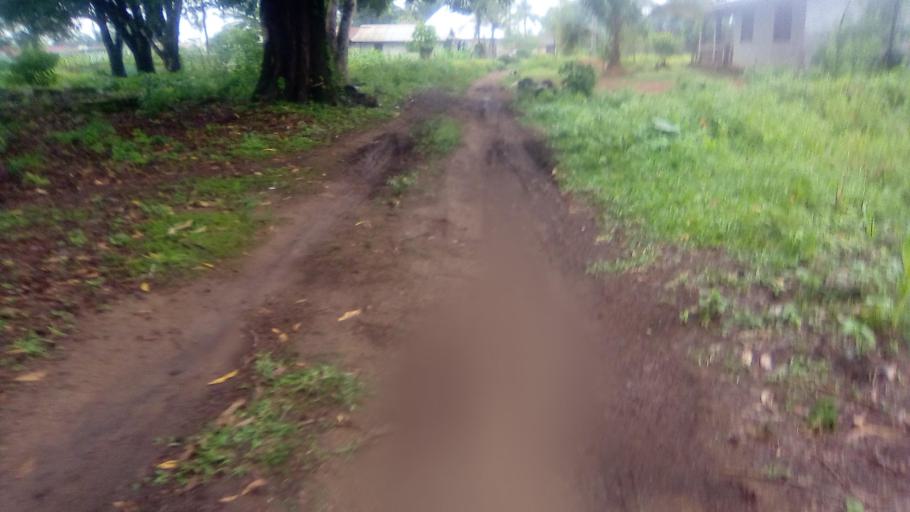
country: SL
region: Southern Province
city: Moyamba
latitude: 8.1503
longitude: -12.4318
